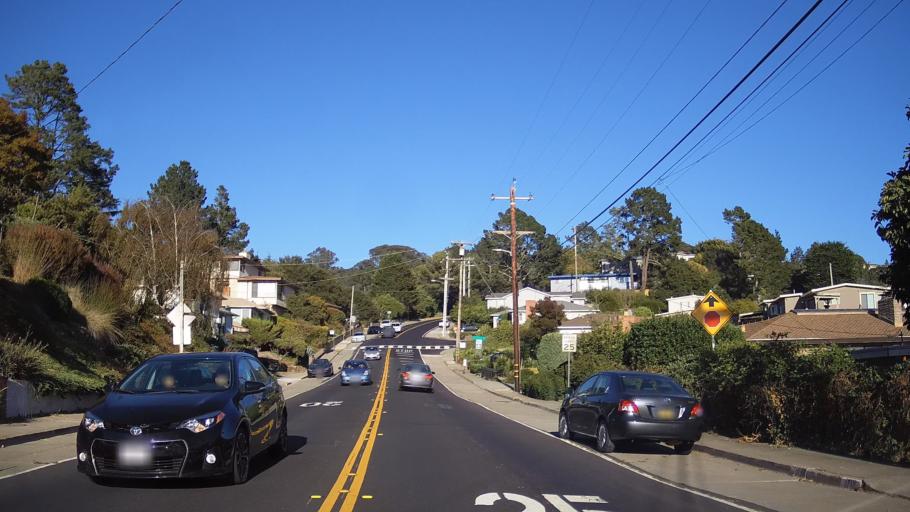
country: US
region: California
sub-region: Contra Costa County
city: El Cerrito
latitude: 37.9295
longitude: -122.3056
